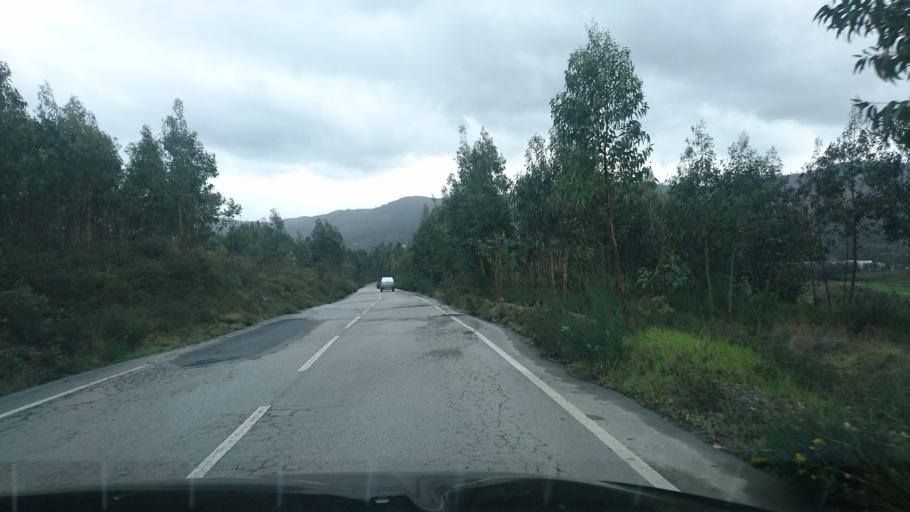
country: PT
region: Porto
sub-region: Paredes
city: Recarei
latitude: 41.1295
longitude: -8.4031
